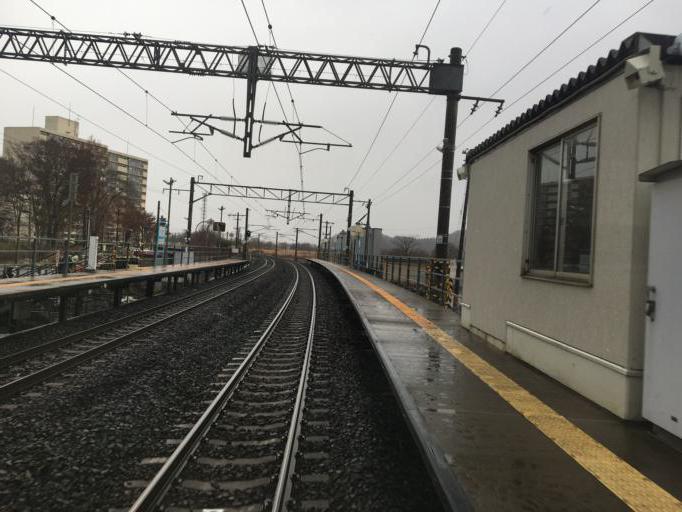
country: JP
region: Aomori
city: Aomori Shi
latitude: 40.8179
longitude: 140.7978
